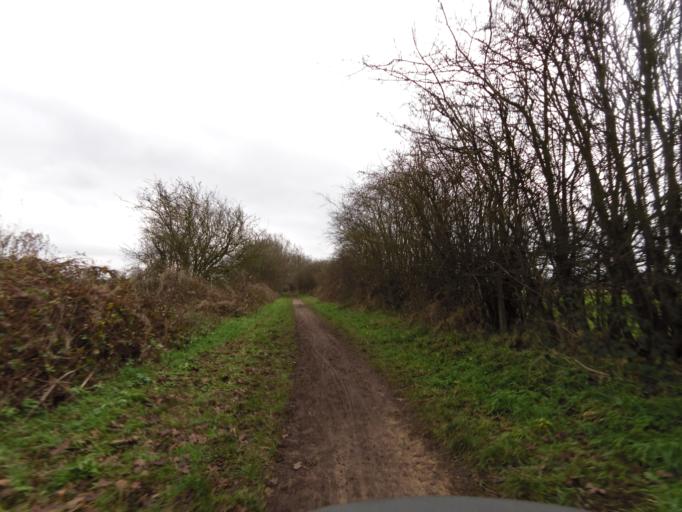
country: GB
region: England
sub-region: Norfolk
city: Mattishall
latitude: 52.7306
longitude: 1.1033
